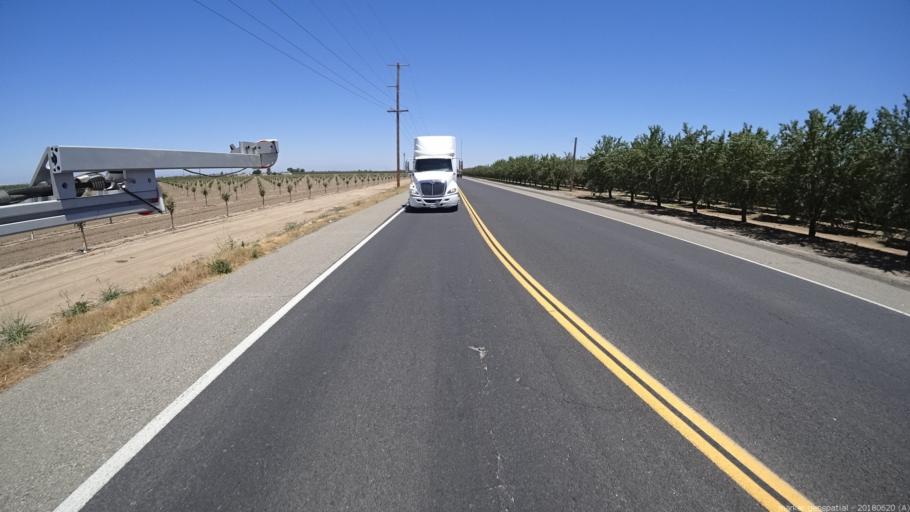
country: US
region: California
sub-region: Madera County
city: Parkwood
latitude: 36.9239
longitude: -120.0827
